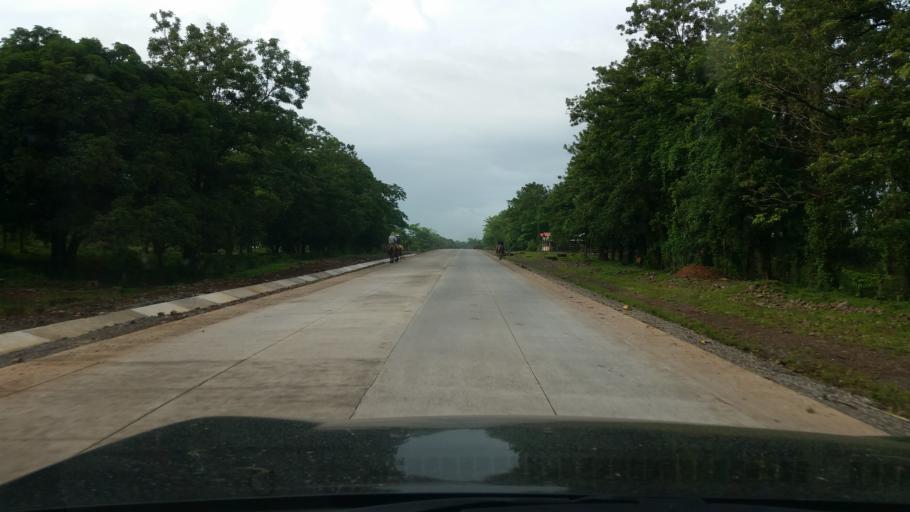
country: NI
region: Matagalpa
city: Rio Blanco
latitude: 13.1117
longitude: -85.0642
